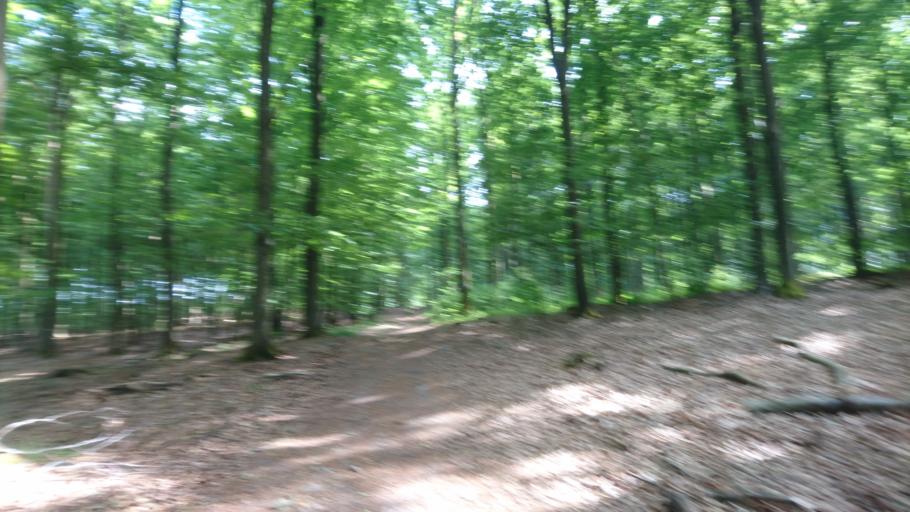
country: SE
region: Skane
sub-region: Lunds Kommun
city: Veberod
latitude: 55.6233
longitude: 13.4371
